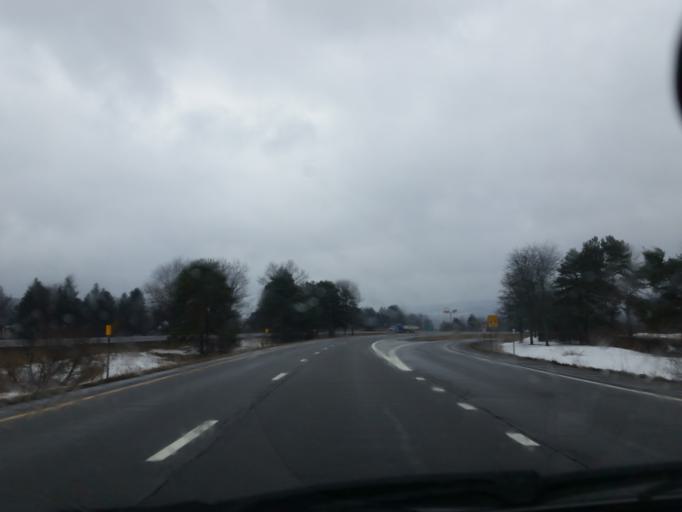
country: US
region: New York
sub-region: Chenango County
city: Lakeview
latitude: 42.3435
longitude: -75.9803
